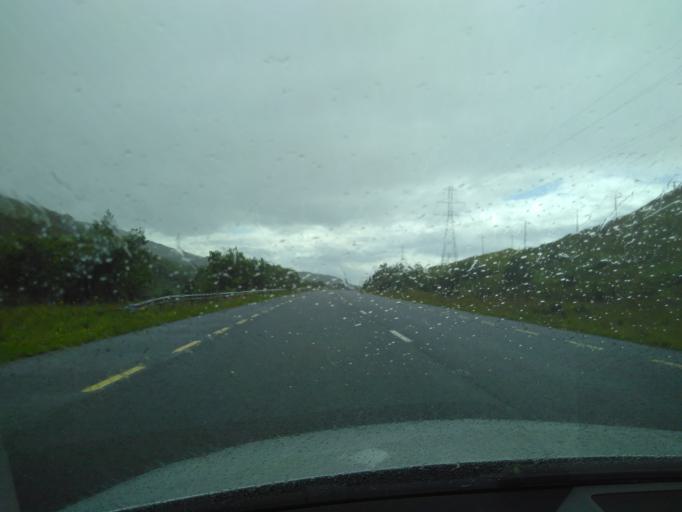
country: IE
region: Ulster
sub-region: County Donegal
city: Donegal
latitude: 54.7153
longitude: -7.9620
